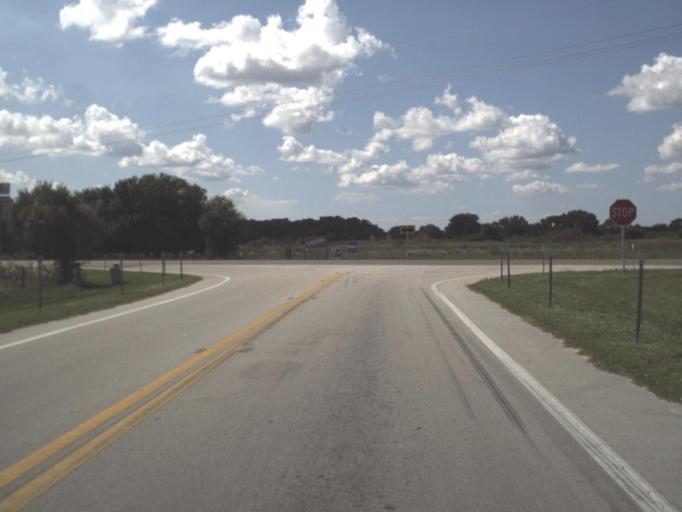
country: US
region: Florida
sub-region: Hendry County
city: Port LaBelle
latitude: 26.8125
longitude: -81.4121
